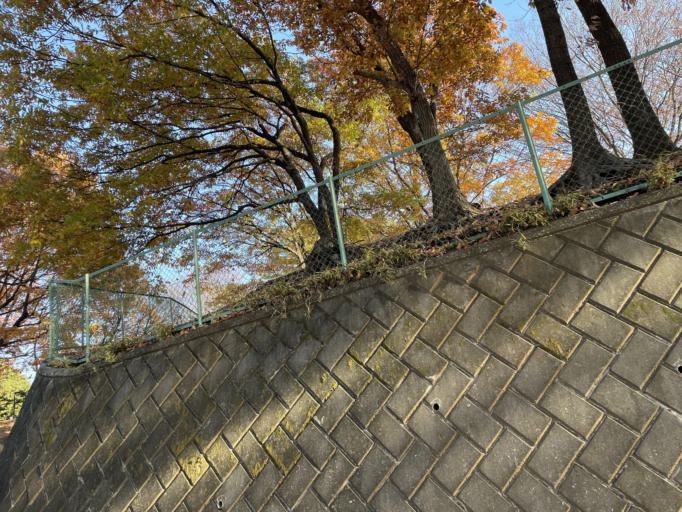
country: JP
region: Saitama
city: Asaka
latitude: 35.7832
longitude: 139.5803
